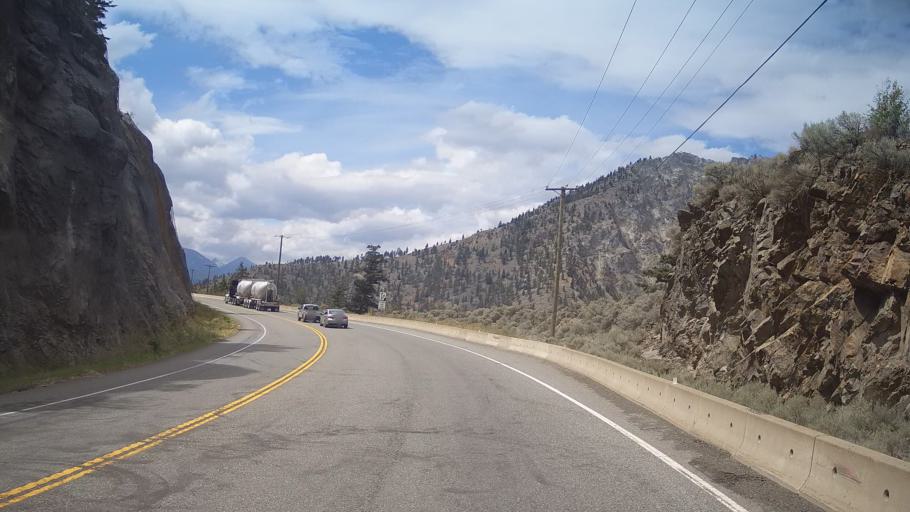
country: CA
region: British Columbia
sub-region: Thompson-Nicola Regional District
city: Ashcroft
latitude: 50.2578
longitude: -121.4615
